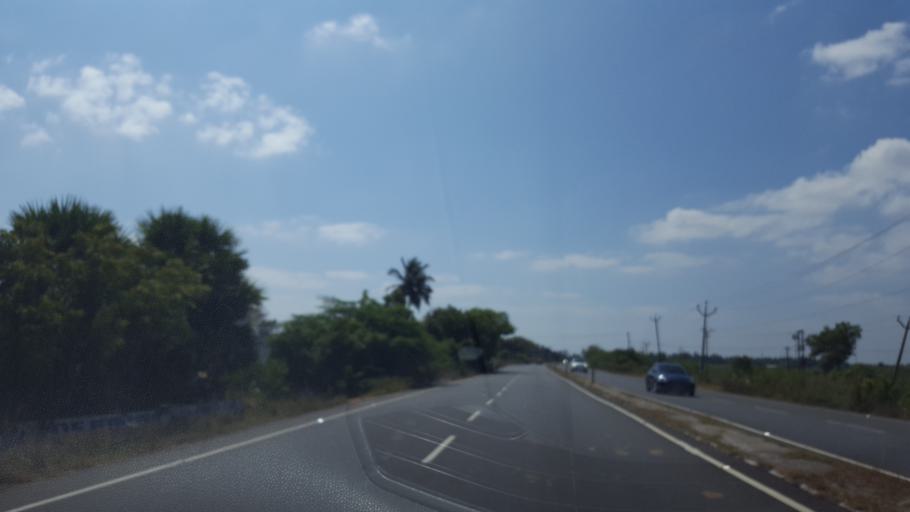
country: IN
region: Tamil Nadu
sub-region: Kancheepuram
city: Mamallapuram
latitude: 12.6350
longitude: 80.1719
